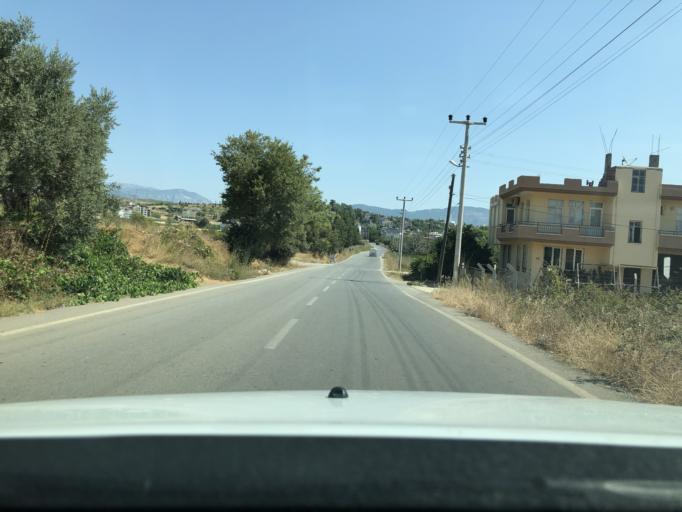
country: TR
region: Antalya
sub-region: Manavgat
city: Manavgat
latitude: 36.8063
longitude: 31.4787
